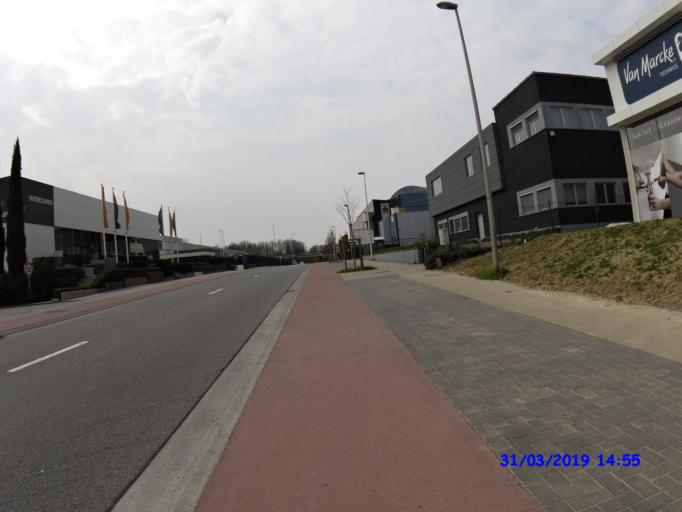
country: BE
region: Flanders
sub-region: Provincie Vlaams-Brabant
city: Dilbeek
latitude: 50.8724
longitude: 4.2756
